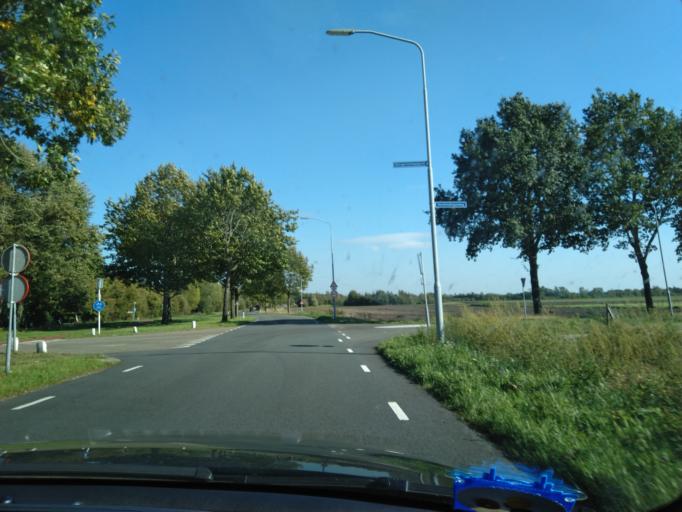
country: NL
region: Groningen
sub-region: Gemeente Veendam
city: Veendam
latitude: 53.0912
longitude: 6.8338
